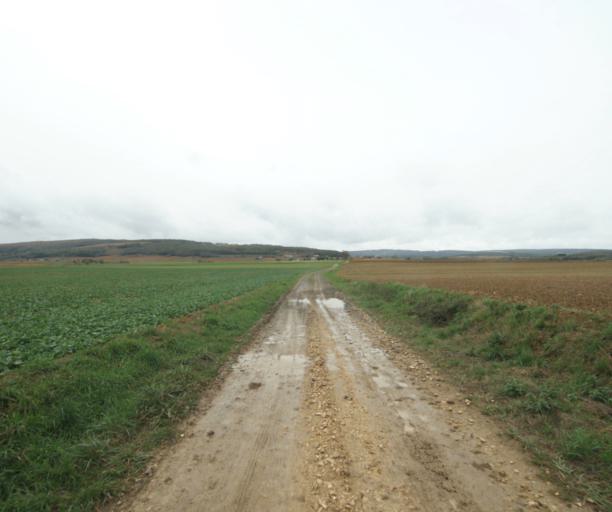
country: FR
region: Rhone-Alpes
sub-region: Departement de l'Ain
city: Pont-de-Vaux
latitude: 46.4675
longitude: 4.8697
